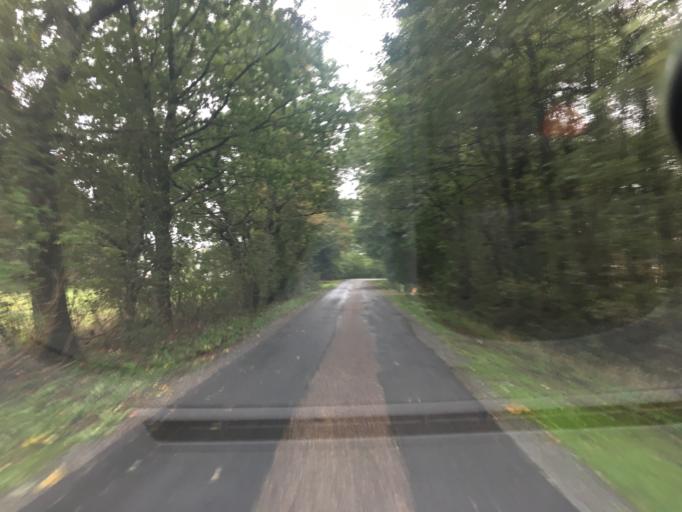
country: DE
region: Schleswig-Holstein
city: Ellhoft
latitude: 54.9504
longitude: 9.0159
